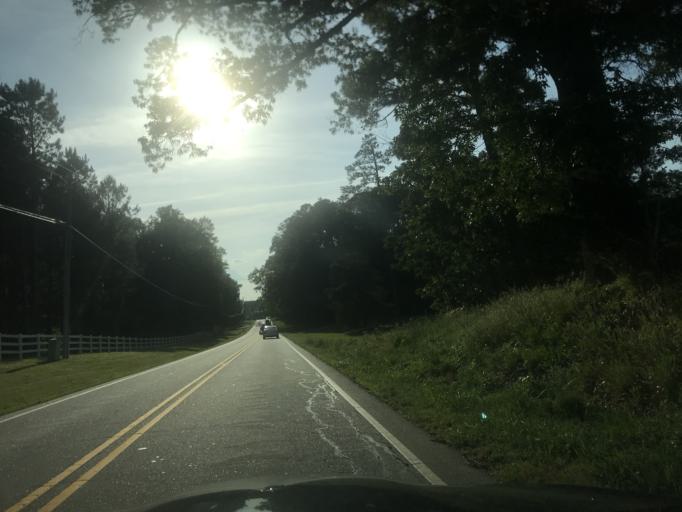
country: US
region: North Carolina
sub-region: Wake County
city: Knightdale
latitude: 35.7473
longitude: -78.4530
